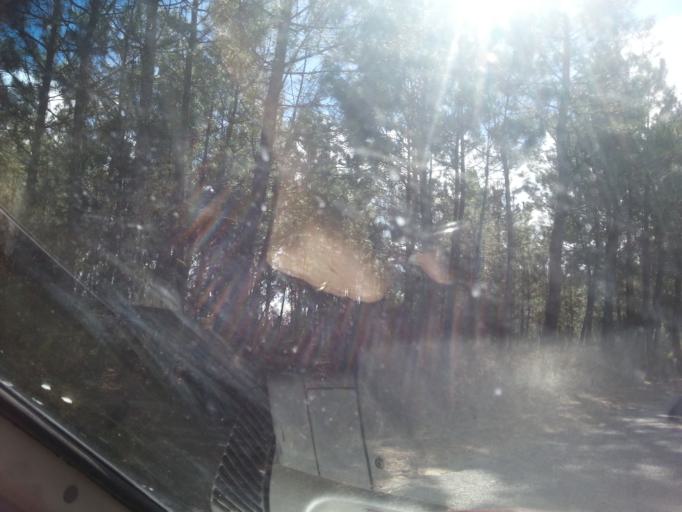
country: PT
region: Guarda
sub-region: Fornos de Algodres
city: Fornos de Algodres
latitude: 40.6596
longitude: -7.5070
